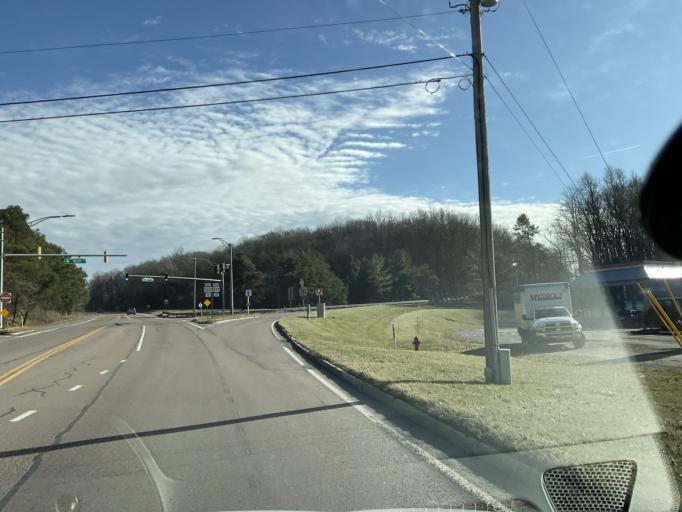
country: US
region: Maryland
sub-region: Garrett County
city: Oakland
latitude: 39.4039
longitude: -79.3991
